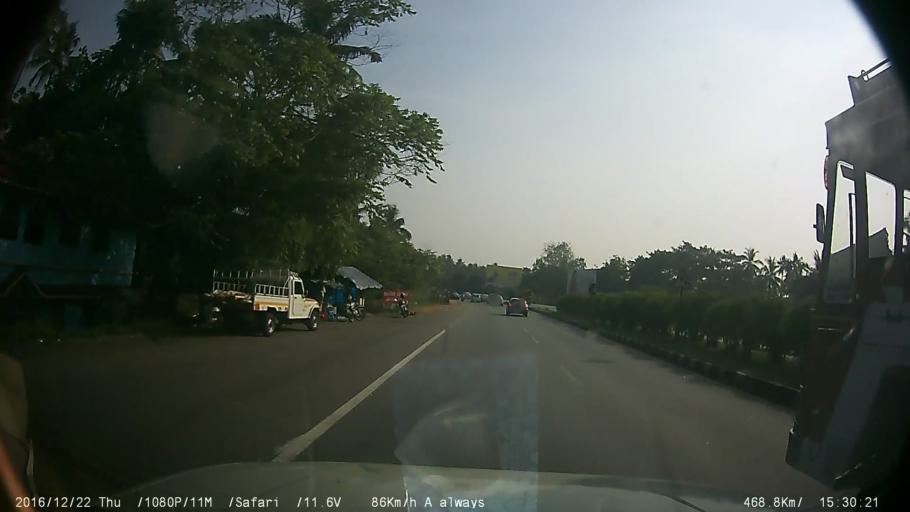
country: IN
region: Kerala
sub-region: Thrissur District
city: Irinjalakuda
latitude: 10.3897
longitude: 76.2885
